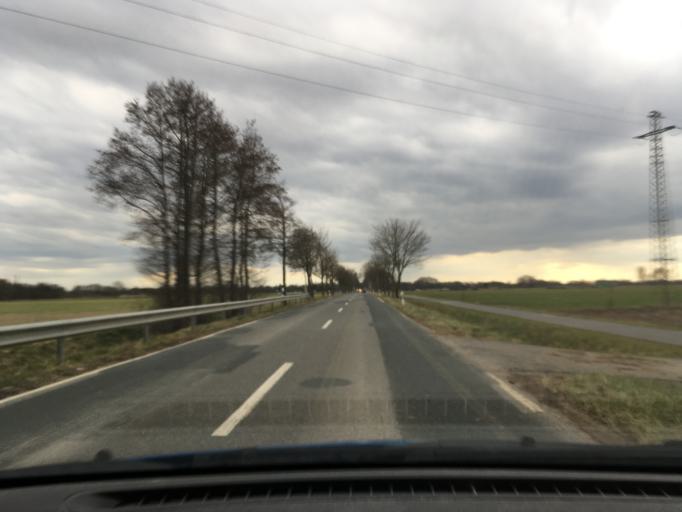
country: DE
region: Lower Saxony
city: Handorf
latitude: 53.3784
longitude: 10.3443
